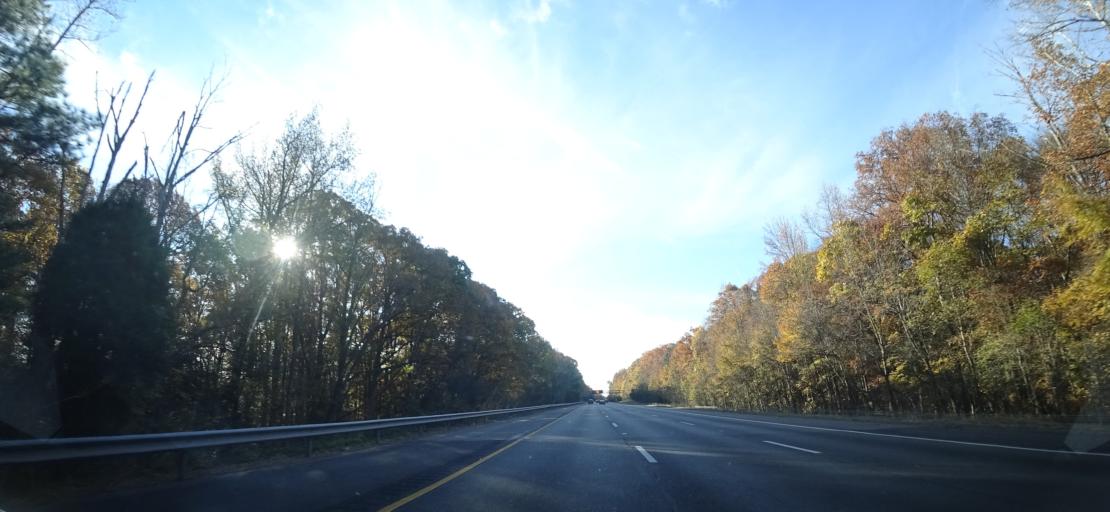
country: US
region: Virginia
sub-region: Hanover County
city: Ashland
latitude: 37.7954
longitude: -77.4607
